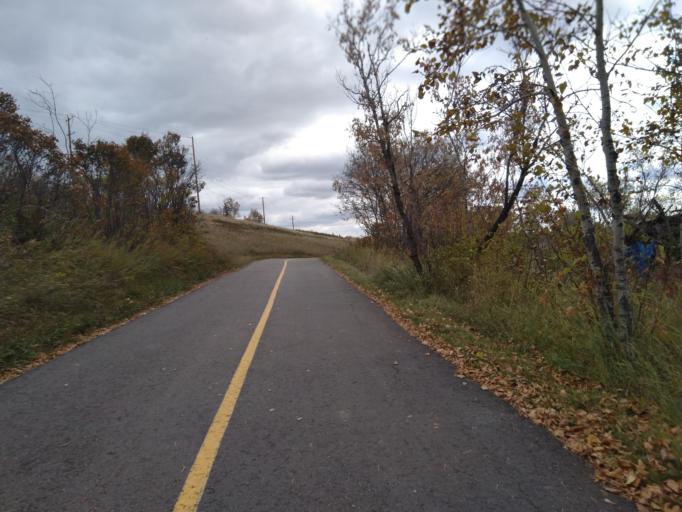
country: CA
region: Alberta
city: Calgary
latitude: 51.0396
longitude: -114.0030
